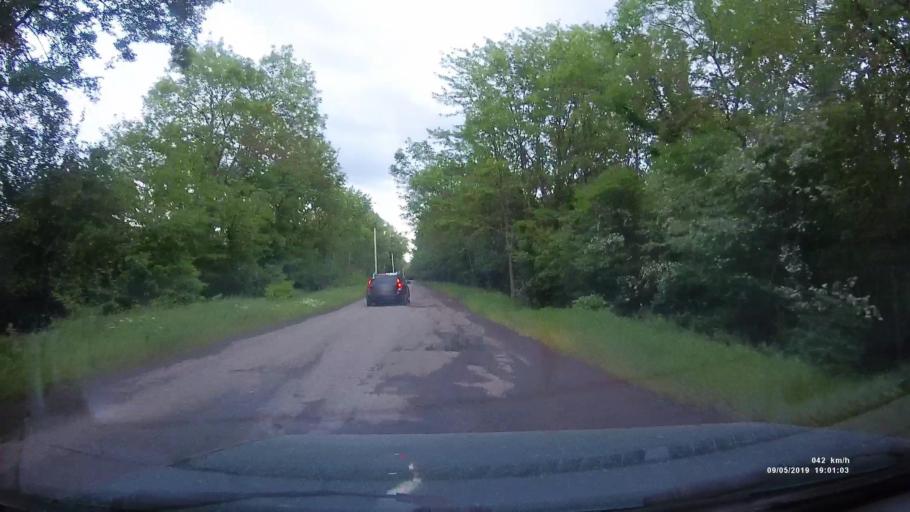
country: RU
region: Krasnodarskiy
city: Kanelovskaya
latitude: 46.7495
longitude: 39.1411
